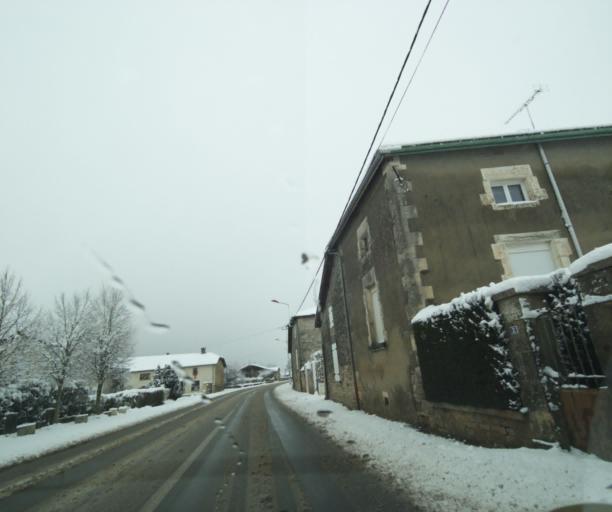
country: FR
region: Champagne-Ardenne
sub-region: Departement de la Haute-Marne
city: Wassy
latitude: 48.5236
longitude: 4.9311
